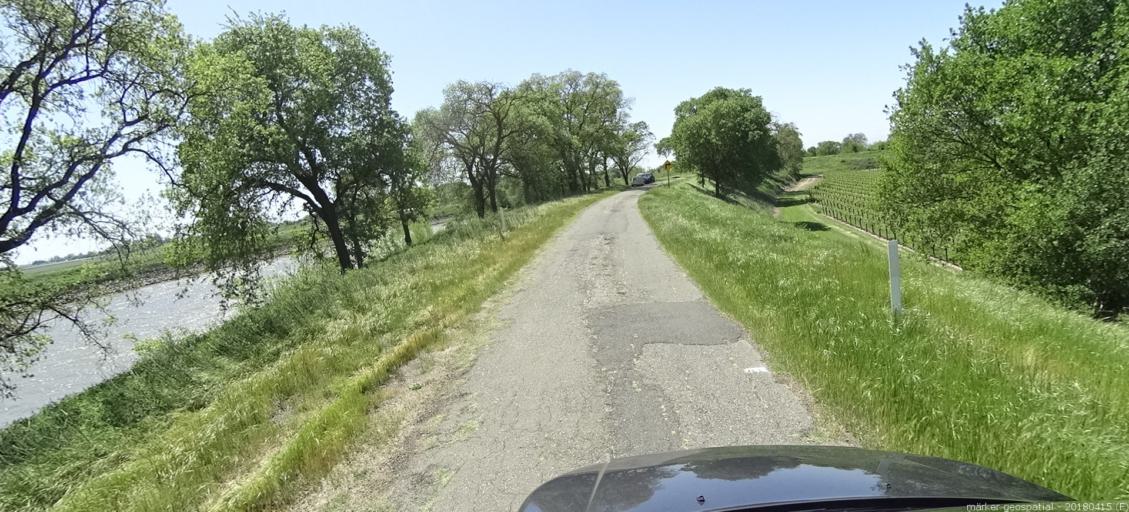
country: US
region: California
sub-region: Sacramento County
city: Walnut Grove
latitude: 38.2555
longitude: -121.5972
